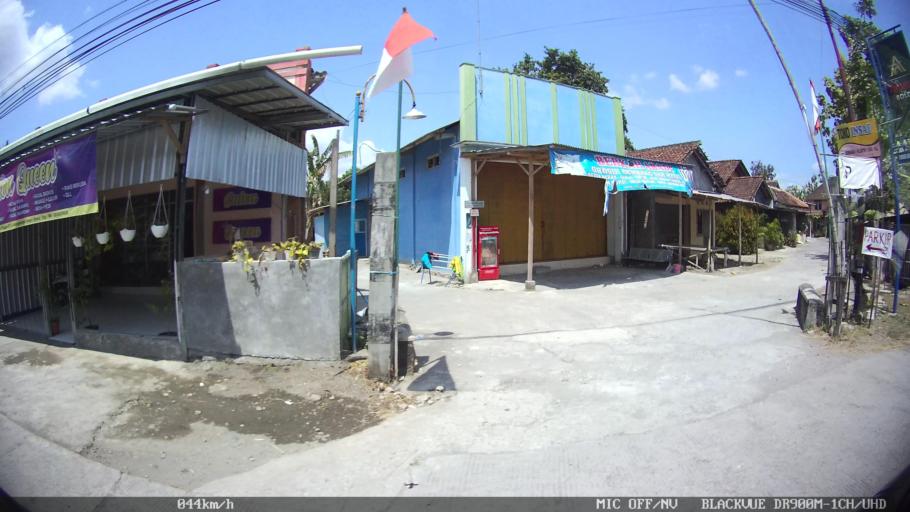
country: ID
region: Daerah Istimewa Yogyakarta
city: Pundong
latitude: -7.9197
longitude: 110.3767
